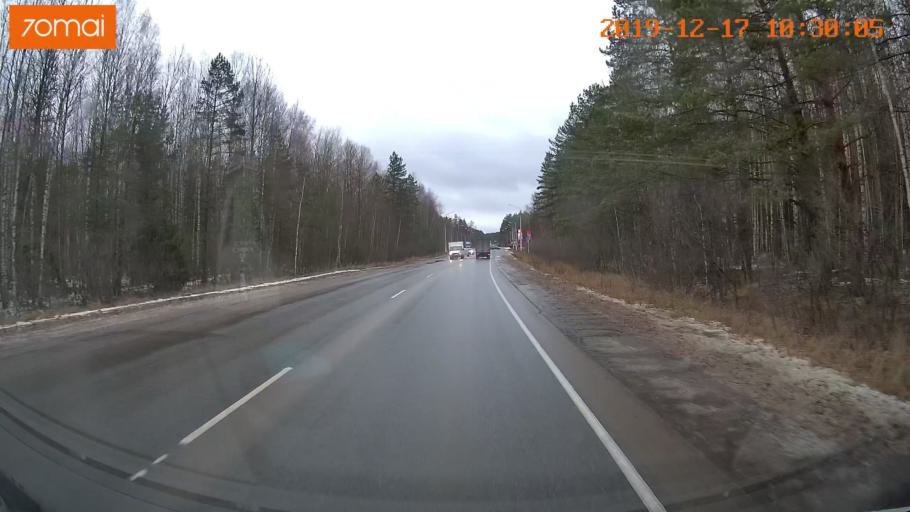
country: RU
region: Vladimir
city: Gus'-Khrustal'nyy
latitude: 55.6453
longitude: 40.7126
